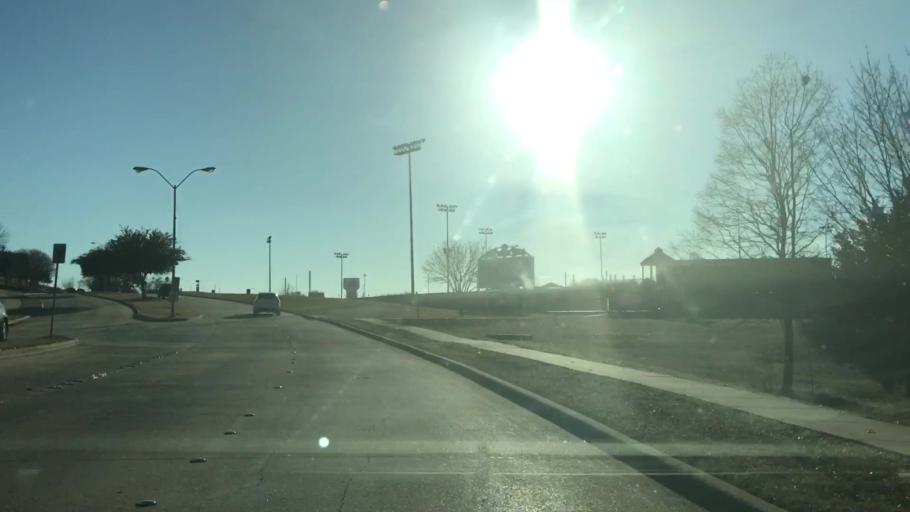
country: US
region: Texas
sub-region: Rockwall County
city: Rockwall
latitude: 32.9080
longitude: -96.4582
